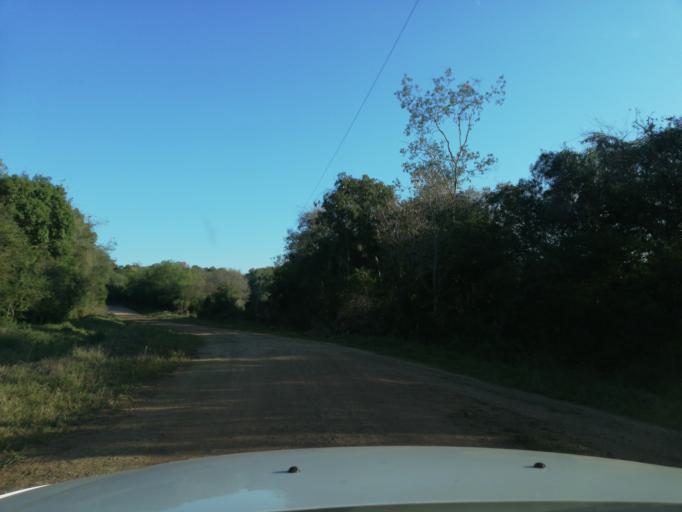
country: AR
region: Misiones
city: Cerro Cora
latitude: -27.6081
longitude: -55.7046
